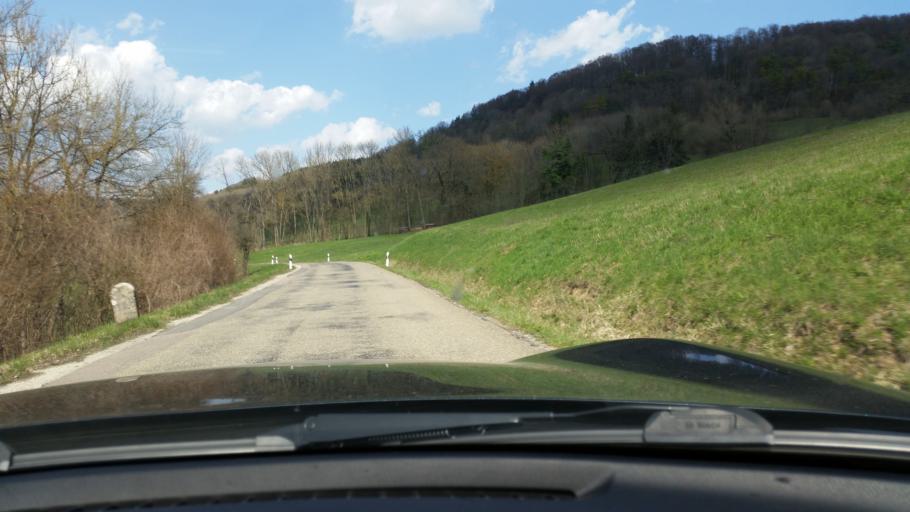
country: DE
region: Baden-Wuerttemberg
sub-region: Regierungsbezirk Stuttgart
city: Langenburg
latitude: 49.2617
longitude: 9.8433
